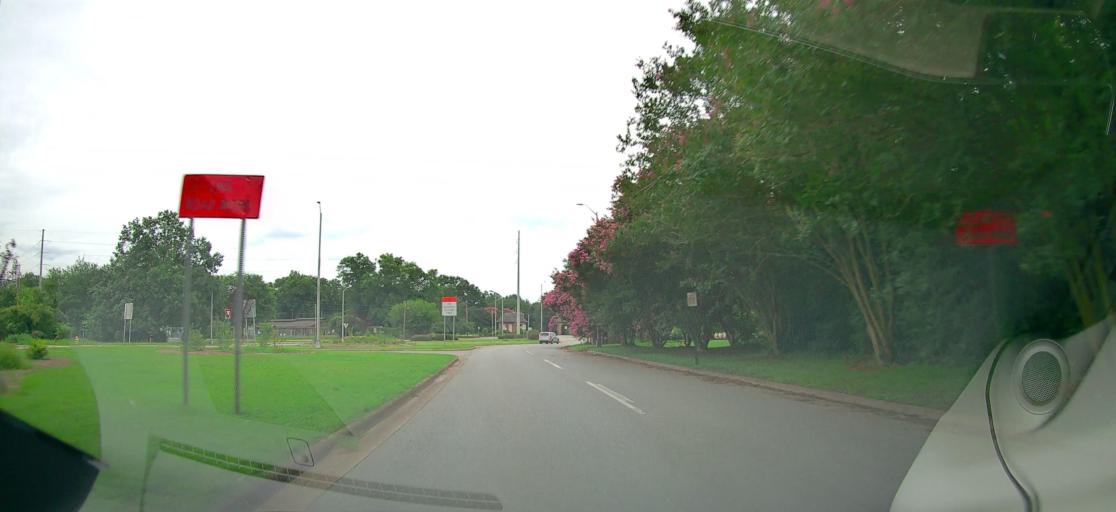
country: US
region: Georgia
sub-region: Bibb County
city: Macon
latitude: 32.8364
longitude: -83.6194
